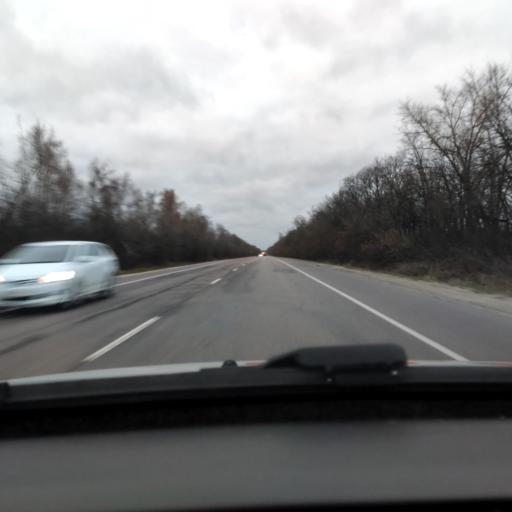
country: RU
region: Lipetsk
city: Khlevnoye
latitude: 52.2887
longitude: 39.1676
